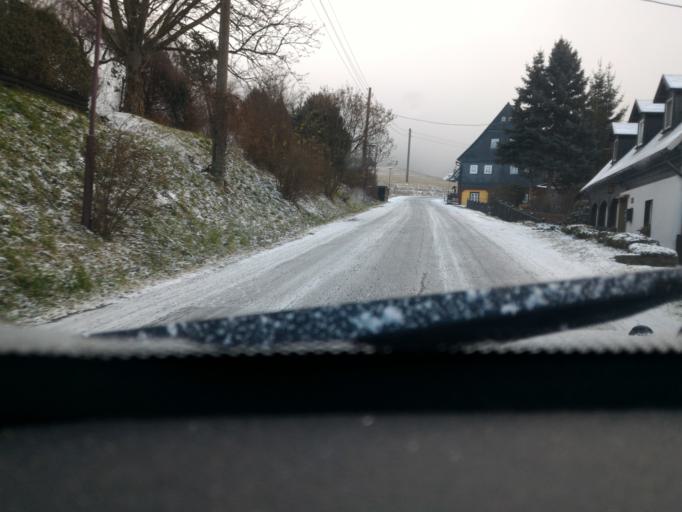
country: DE
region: Saxony
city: Grossschonau
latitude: 50.8614
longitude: 14.6519
